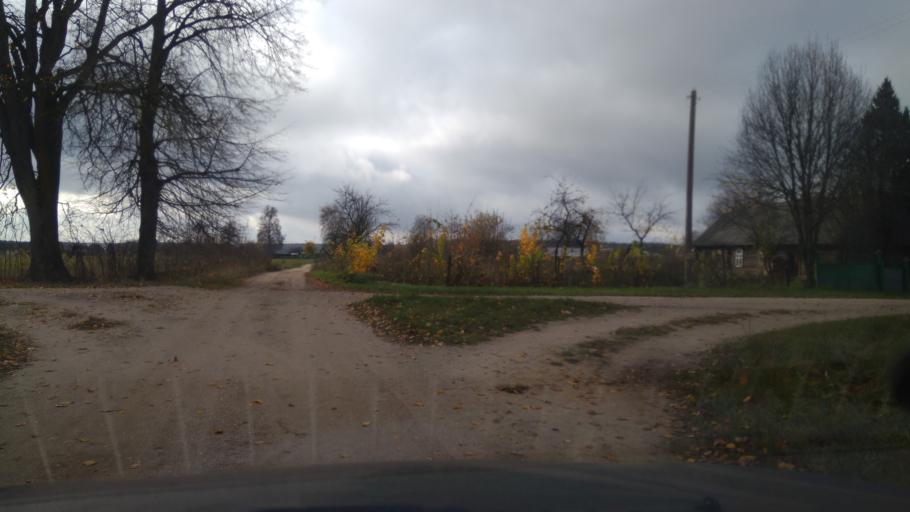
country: BY
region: Minsk
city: Staryya Darohi
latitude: 53.2052
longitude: 28.0466
